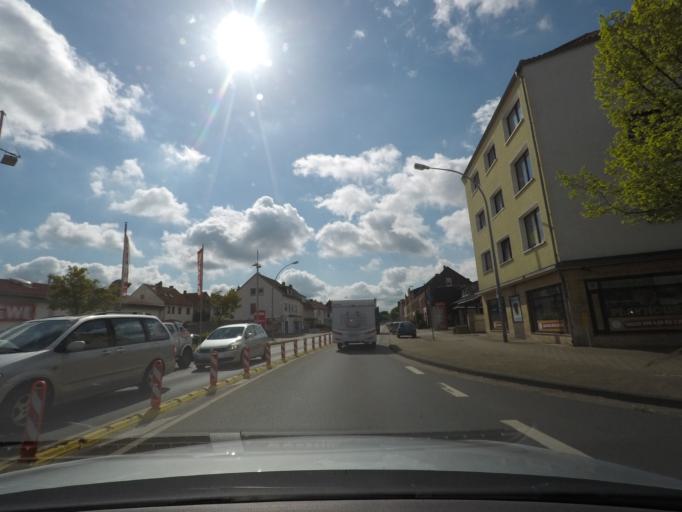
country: DE
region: Lower Saxony
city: Helmstedt
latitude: 52.2370
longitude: 11.0014
